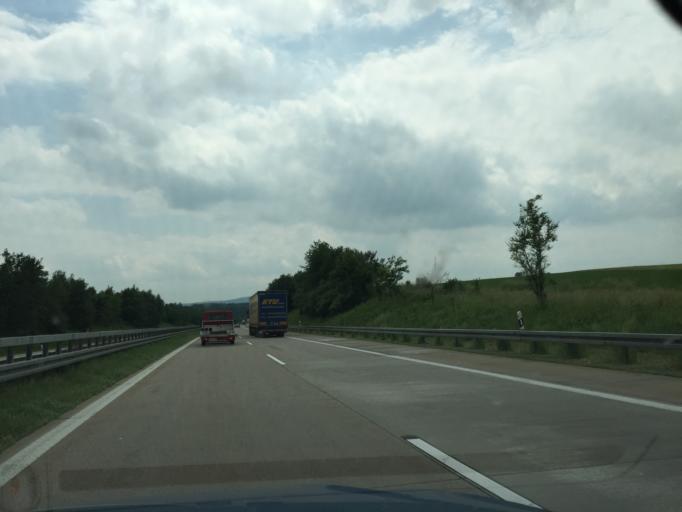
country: DE
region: Baden-Wuerttemberg
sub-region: Regierungsbezirk Stuttgart
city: Westhausen
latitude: 48.9270
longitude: 10.1947
